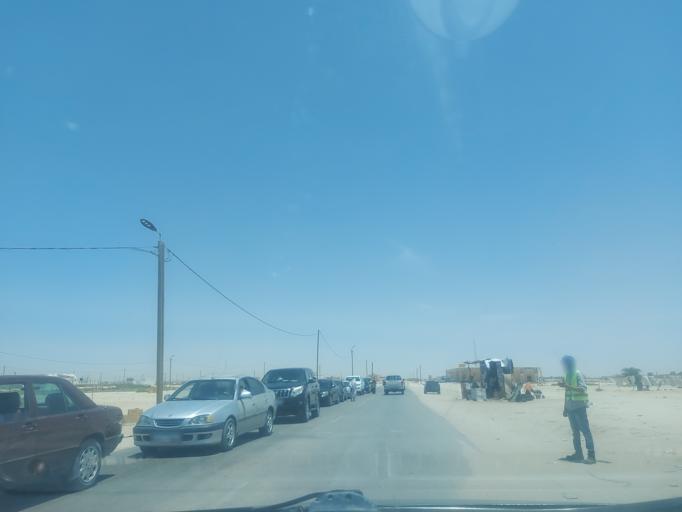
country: MR
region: Nouakchott
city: Nouakchott
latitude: 18.0770
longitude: -15.9557
